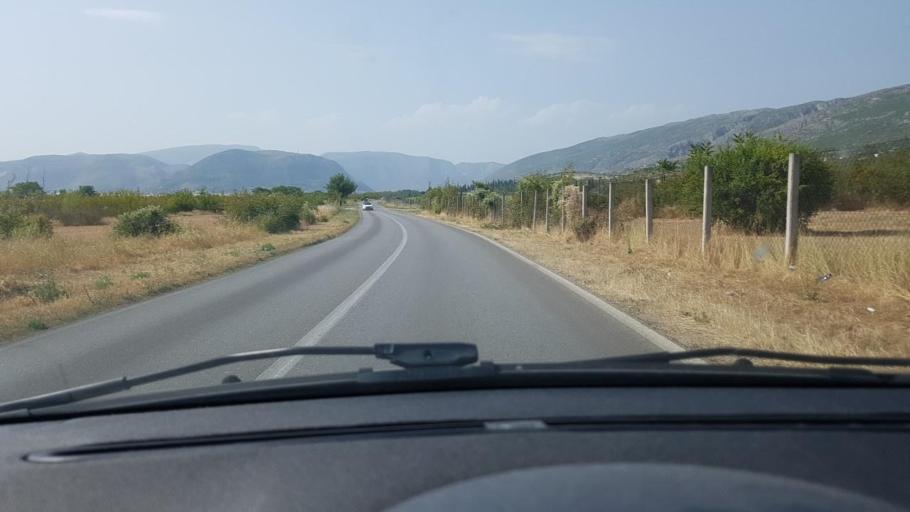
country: BA
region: Federation of Bosnia and Herzegovina
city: Blagaj
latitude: 43.2820
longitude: 17.8524
